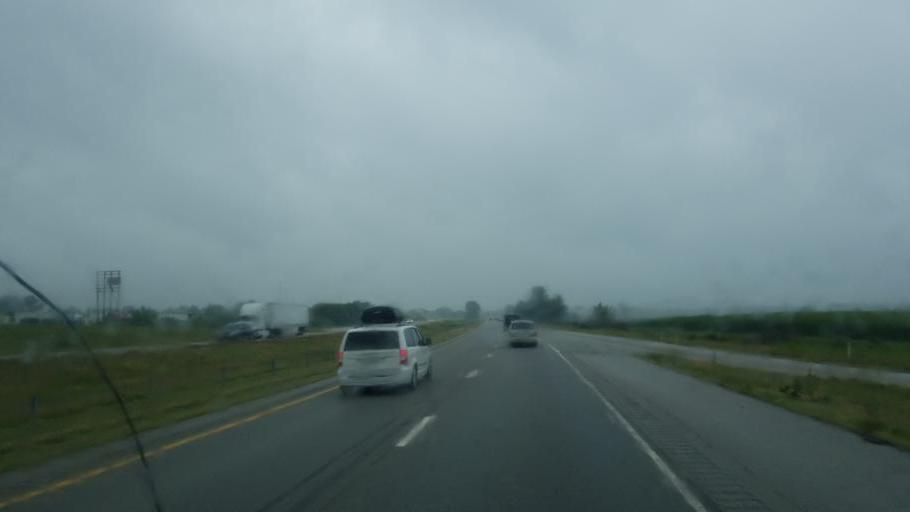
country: US
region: Indiana
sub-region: Morgan County
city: Monrovia
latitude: 39.5699
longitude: -86.6338
